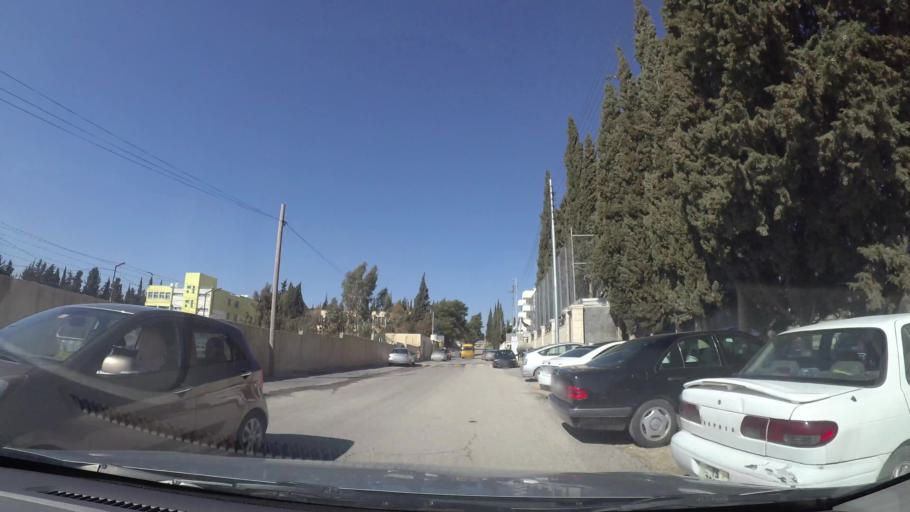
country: JO
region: Amman
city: Al Bunayyat ash Shamaliyah
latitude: 31.9058
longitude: 35.8952
